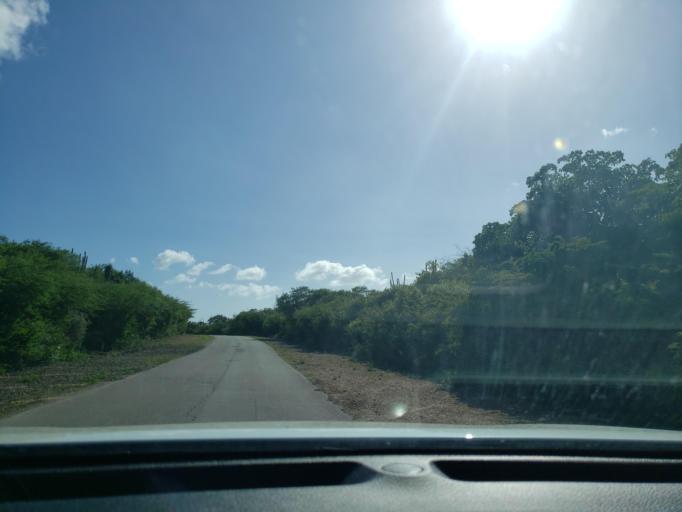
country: CW
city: Dorp Soto
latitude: 12.3488
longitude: -69.1529
